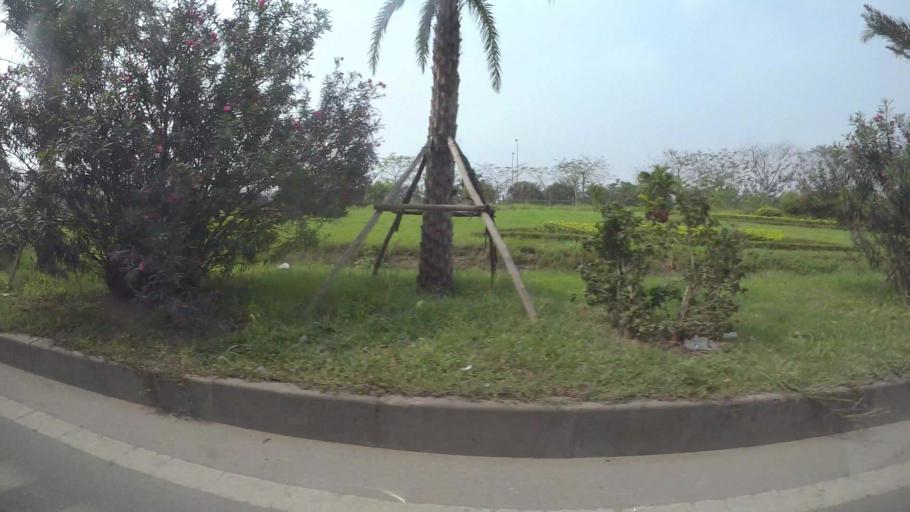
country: VN
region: Ha Noi
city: Thanh Xuan
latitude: 21.0044
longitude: 105.7759
